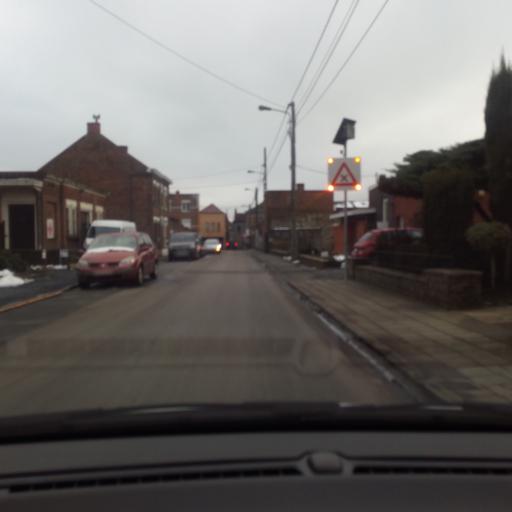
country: BE
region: Wallonia
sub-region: Province du Hainaut
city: Dour
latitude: 50.4006
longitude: 3.7845
